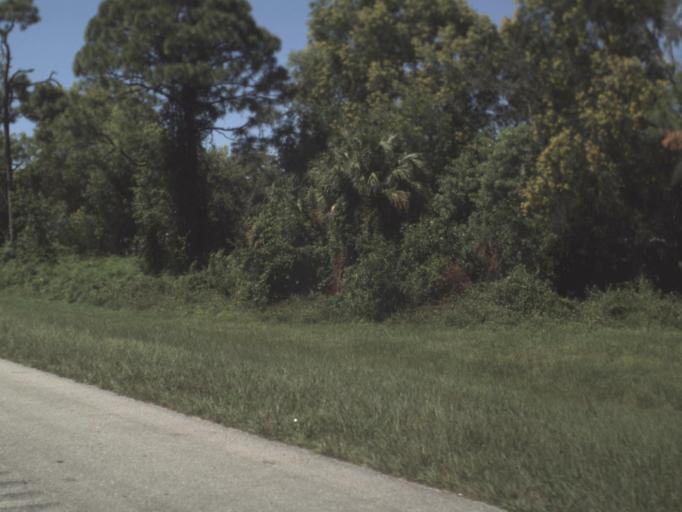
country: US
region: Florida
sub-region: Collier County
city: Golden Gate
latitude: 26.1645
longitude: -81.7134
